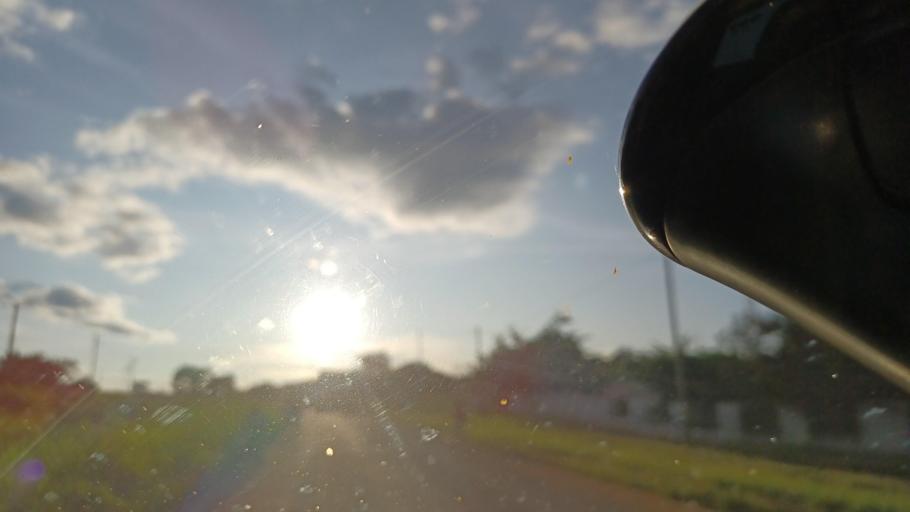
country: ZM
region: North-Western
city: Kasempa
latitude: -13.4582
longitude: 25.8443
